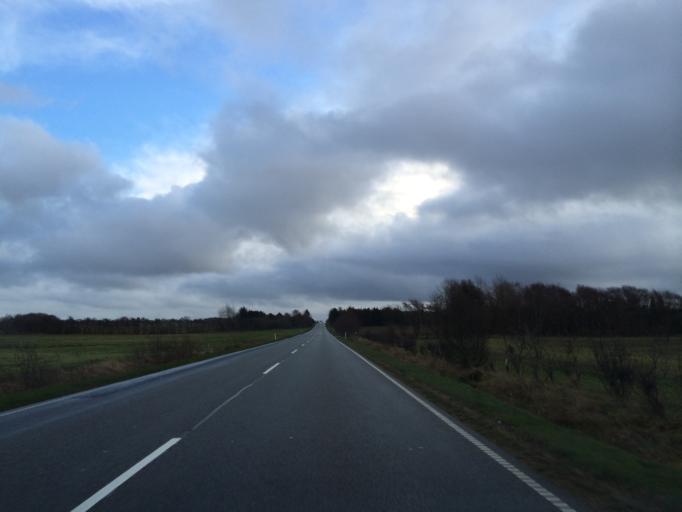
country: DK
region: Central Jutland
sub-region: Ringkobing-Skjern Kommune
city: Ringkobing
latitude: 56.0783
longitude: 8.3624
